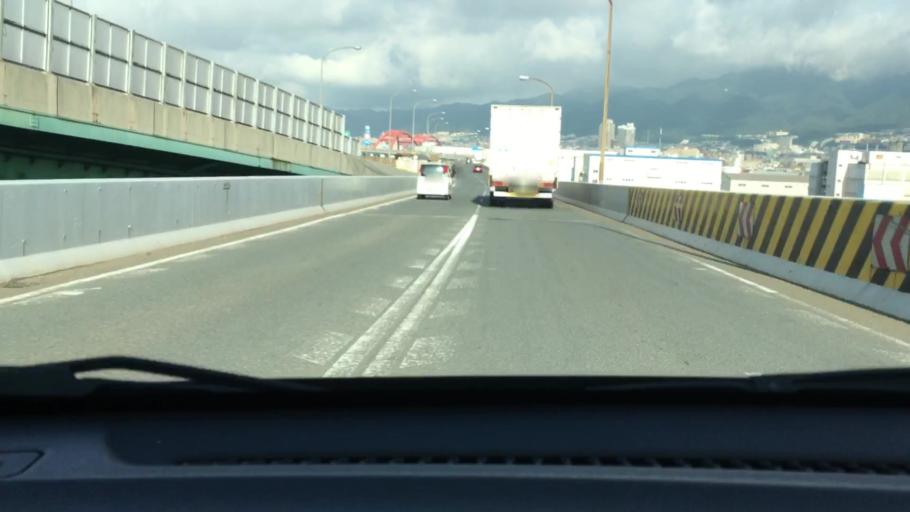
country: JP
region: Hyogo
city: Ashiya
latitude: 34.7058
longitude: 135.2656
